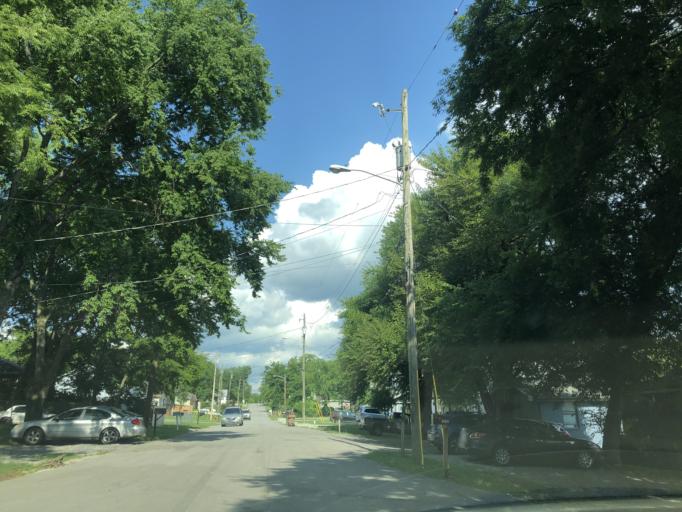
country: US
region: Tennessee
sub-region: Davidson County
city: Nashville
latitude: 36.2067
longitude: -86.7658
